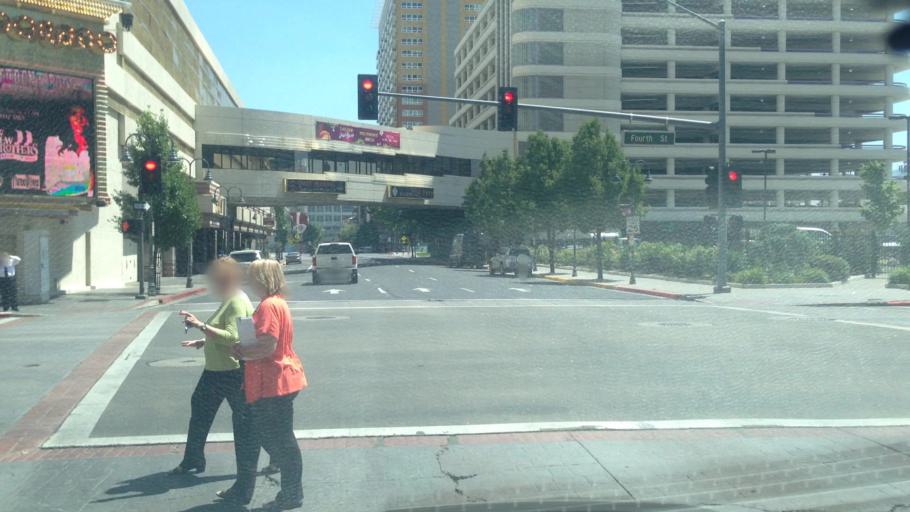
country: US
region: Nevada
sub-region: Washoe County
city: Reno
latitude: 39.5298
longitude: -119.8156
